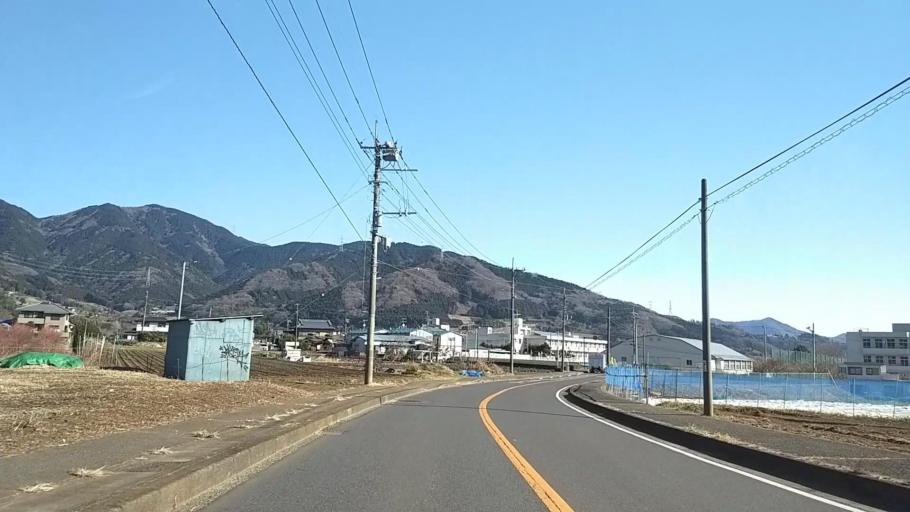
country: JP
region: Kanagawa
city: Hadano
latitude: 35.3990
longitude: 139.1863
